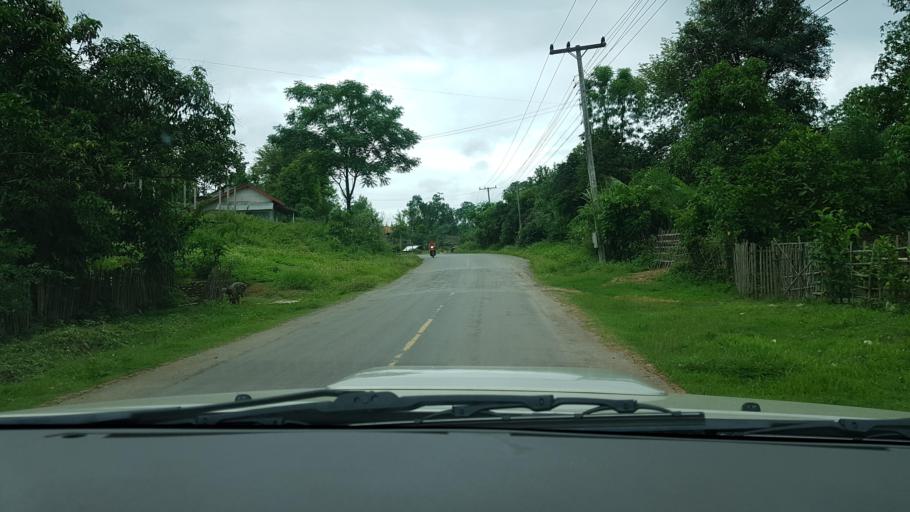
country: LA
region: Loungnamtha
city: Muang Nale
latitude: 20.3109
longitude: 101.6514
